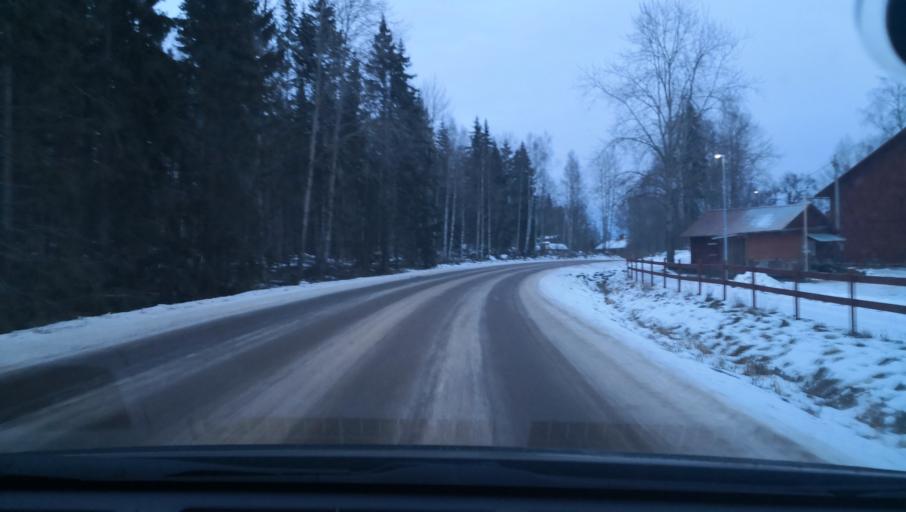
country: SE
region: Dalarna
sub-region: Avesta Kommun
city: Horndal
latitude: 60.1999
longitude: 16.4619
